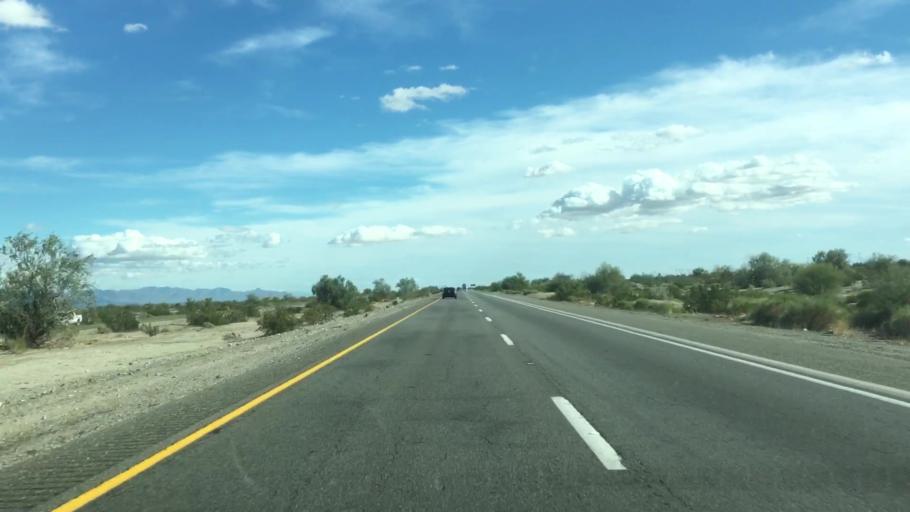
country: US
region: California
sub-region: Imperial County
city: Niland
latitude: 33.6950
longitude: -115.2865
